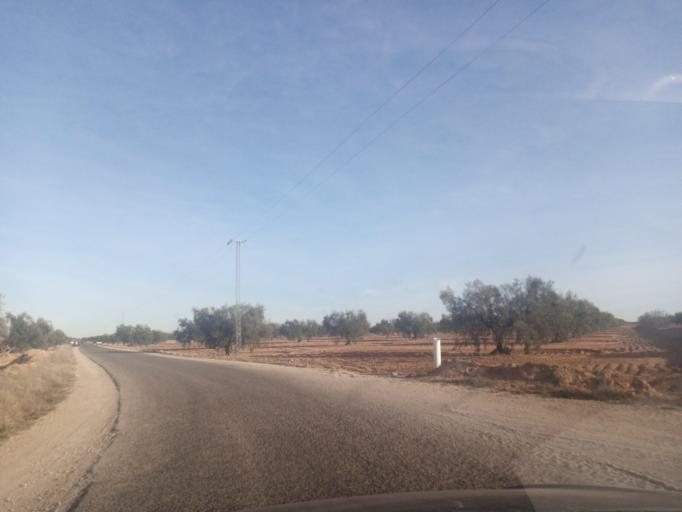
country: TN
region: Safaqis
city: Bi'r `Ali Bin Khalifah
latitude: 34.8875
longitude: 10.1819
